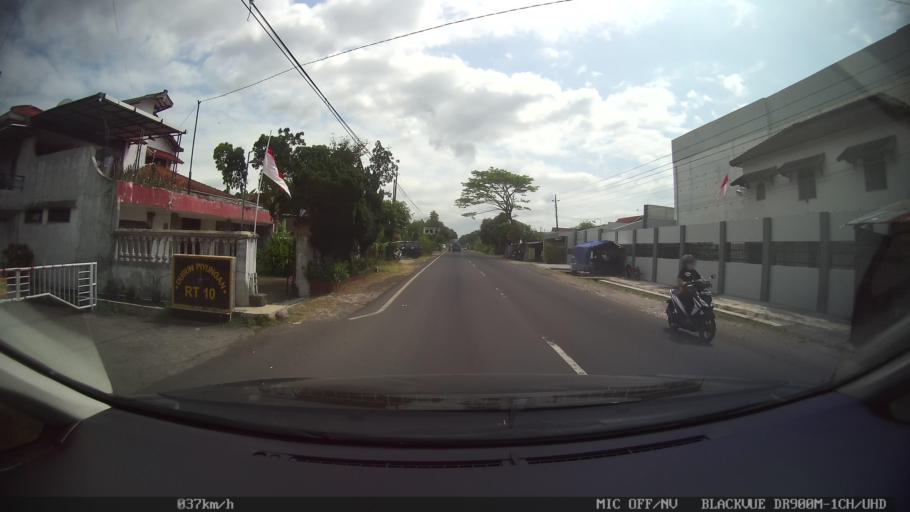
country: ID
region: Daerah Istimewa Yogyakarta
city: Depok
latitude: -7.8334
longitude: 110.4773
